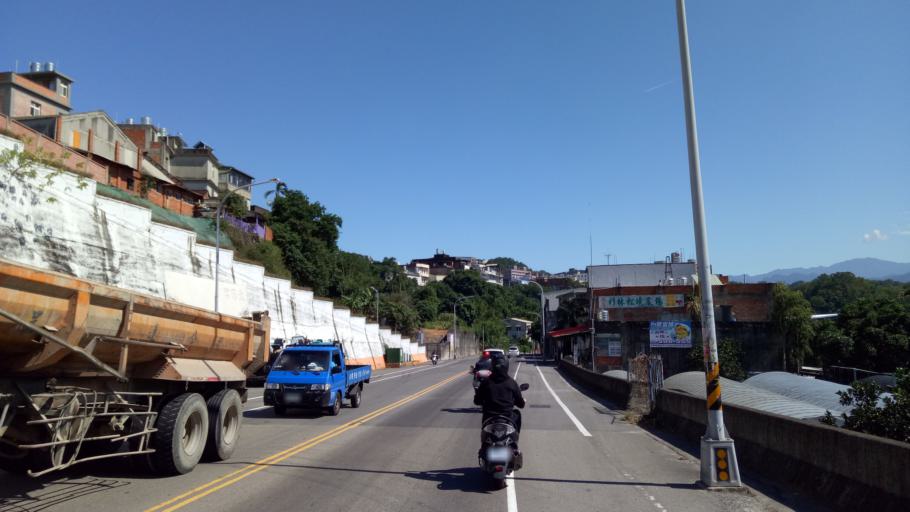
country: TW
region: Taiwan
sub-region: Hsinchu
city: Hsinchu
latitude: 24.6842
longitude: 120.9600
